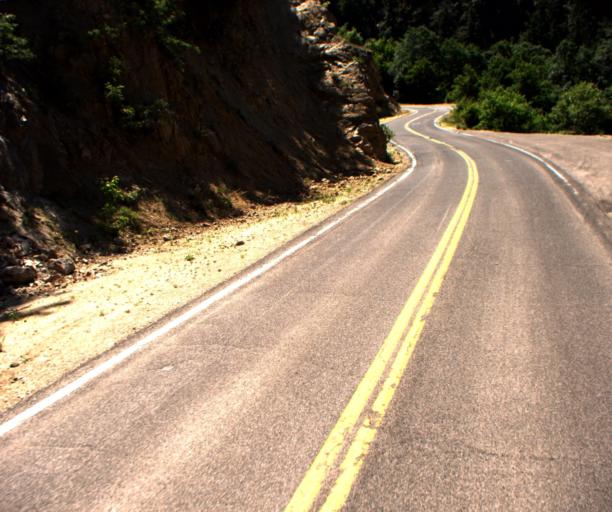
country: US
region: Arizona
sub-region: Graham County
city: Swift Trail Junction
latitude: 32.6358
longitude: -109.8229
